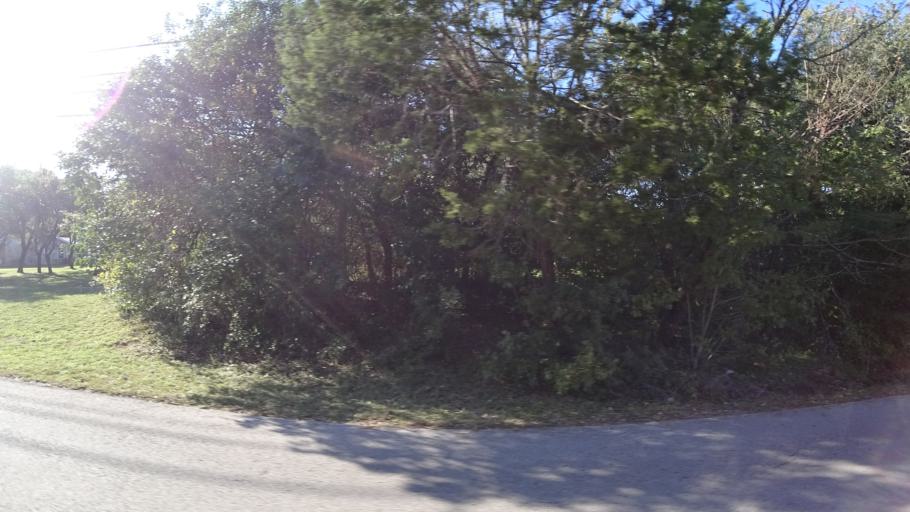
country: US
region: Texas
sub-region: Travis County
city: Barton Creek
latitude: 30.2401
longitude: -97.9080
